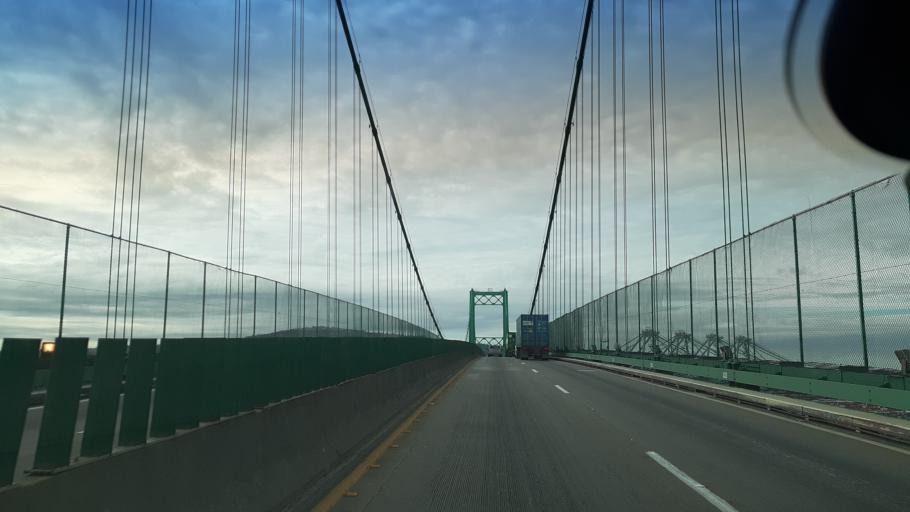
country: US
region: California
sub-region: Los Angeles County
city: San Pedro
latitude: 33.7491
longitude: -118.2693
